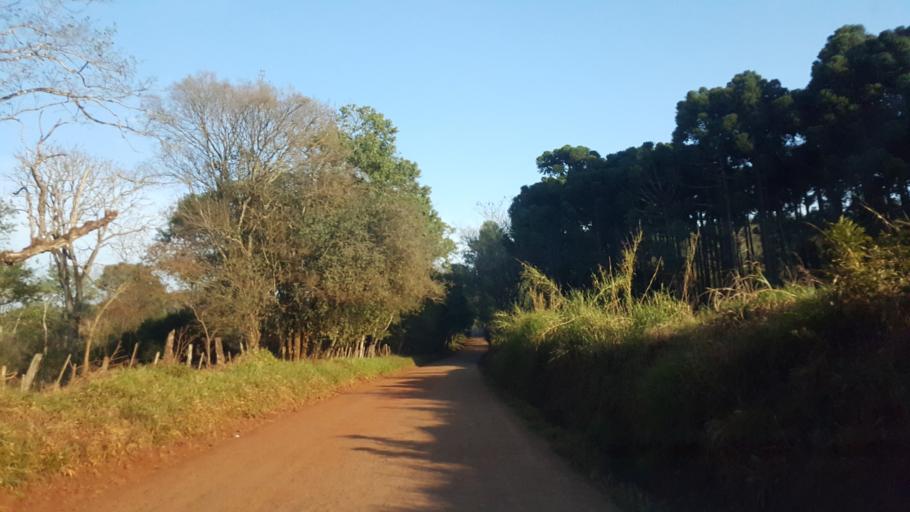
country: AR
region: Misiones
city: Capiovi
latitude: -26.8925
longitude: -55.0600
